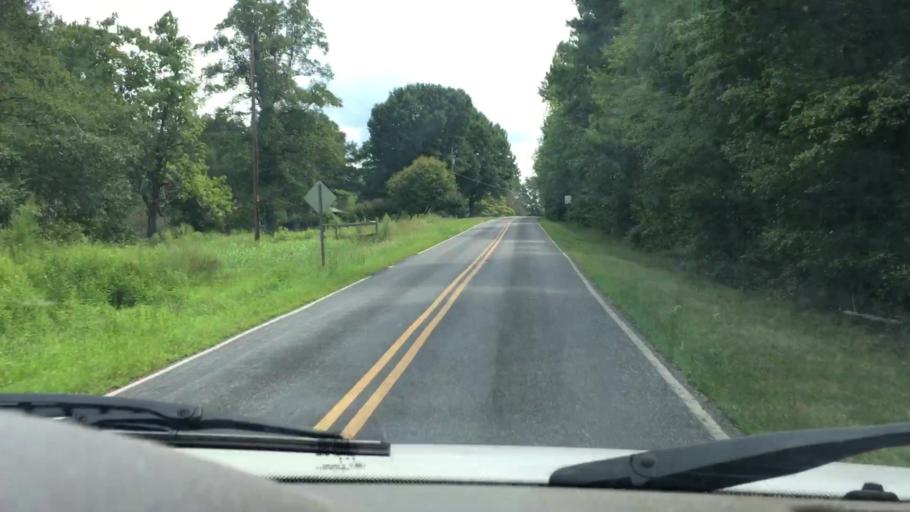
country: US
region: North Carolina
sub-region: Iredell County
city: Mooresville
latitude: 35.6612
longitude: -80.8060
